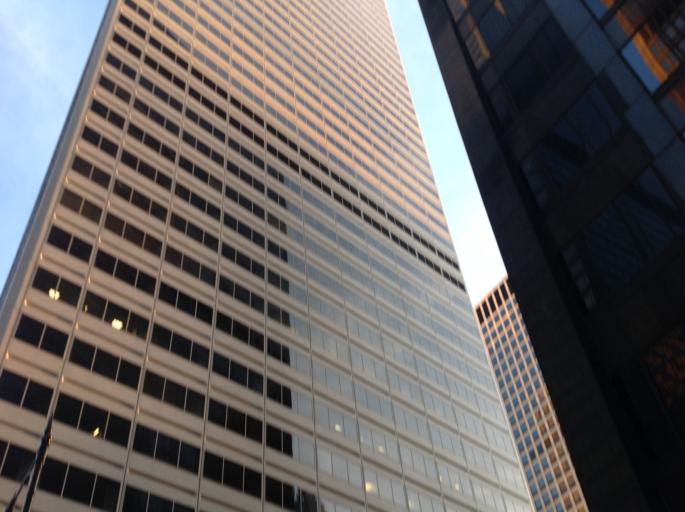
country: US
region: Illinois
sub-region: Cook County
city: Chicago
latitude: 41.8797
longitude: -87.6366
